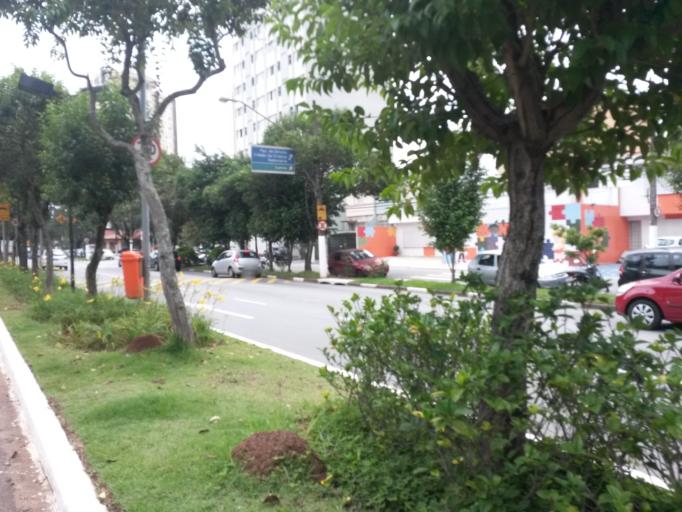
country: BR
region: Sao Paulo
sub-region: Sao Bernardo Do Campo
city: Sao Bernardo do Campo
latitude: -23.6933
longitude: -46.5606
